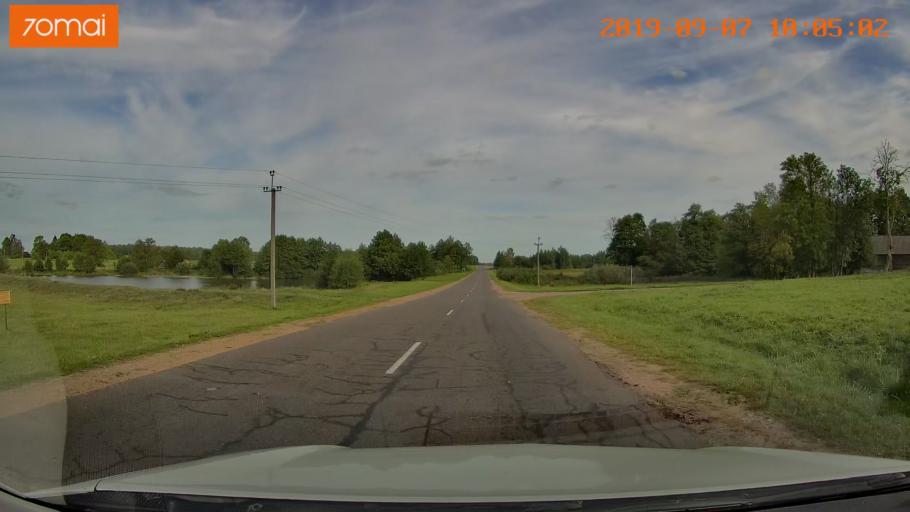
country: BY
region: Grodnenskaya
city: Voranava
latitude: 54.0423
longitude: 25.4093
